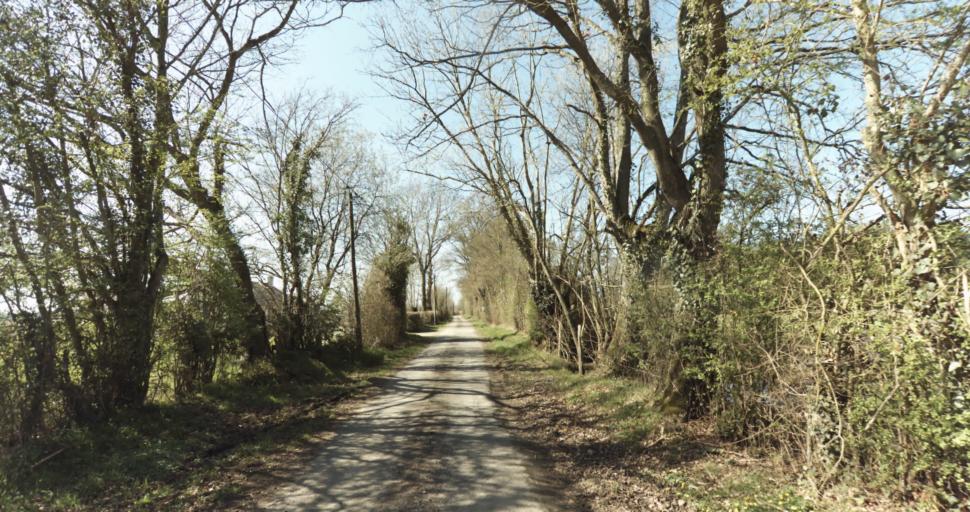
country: FR
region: Lower Normandy
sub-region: Departement du Calvados
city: Livarot
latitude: 49.0213
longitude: 0.0969
